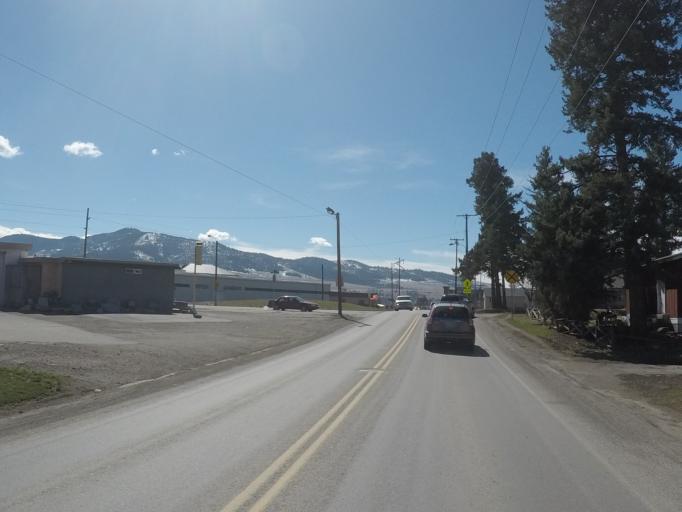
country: US
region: Montana
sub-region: Missoula County
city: Missoula
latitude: 46.8600
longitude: -114.0187
